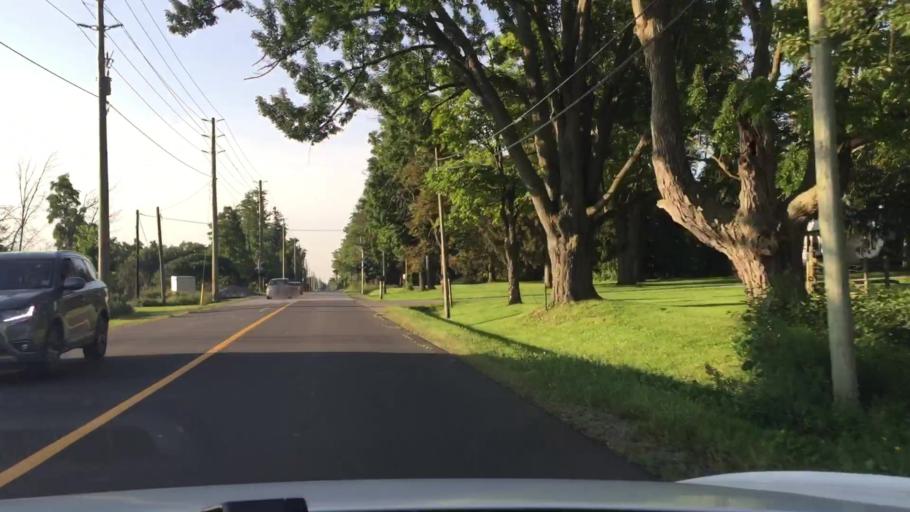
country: CA
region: Ontario
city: Markham
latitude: 43.8730
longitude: -79.2078
